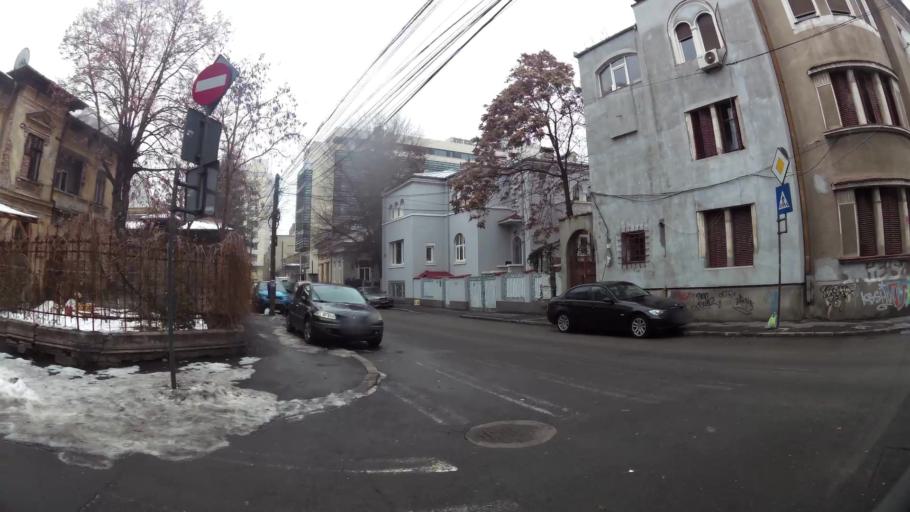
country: RO
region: Bucuresti
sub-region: Municipiul Bucuresti
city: Bucharest
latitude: 44.4415
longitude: 26.1139
